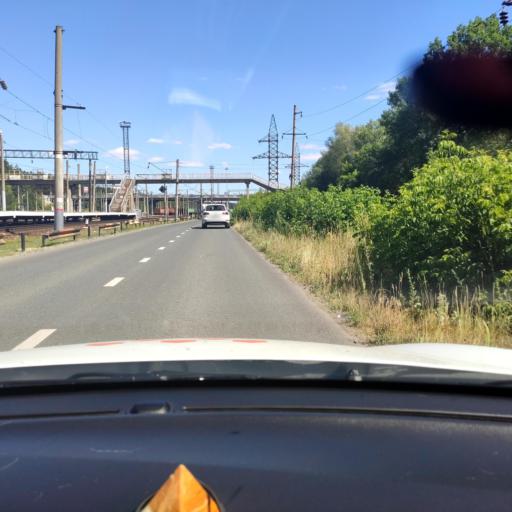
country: RU
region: Tatarstan
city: Osinovo
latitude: 55.8251
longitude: 48.8421
